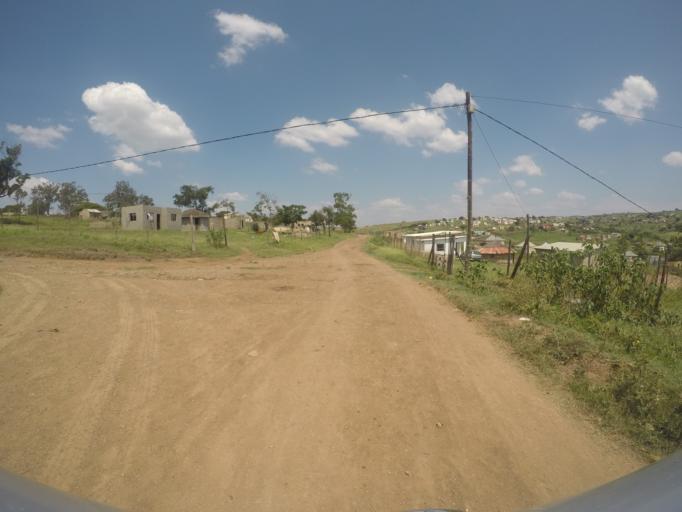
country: ZA
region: KwaZulu-Natal
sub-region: uThungulu District Municipality
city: Empangeni
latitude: -28.6037
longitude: 31.7408
